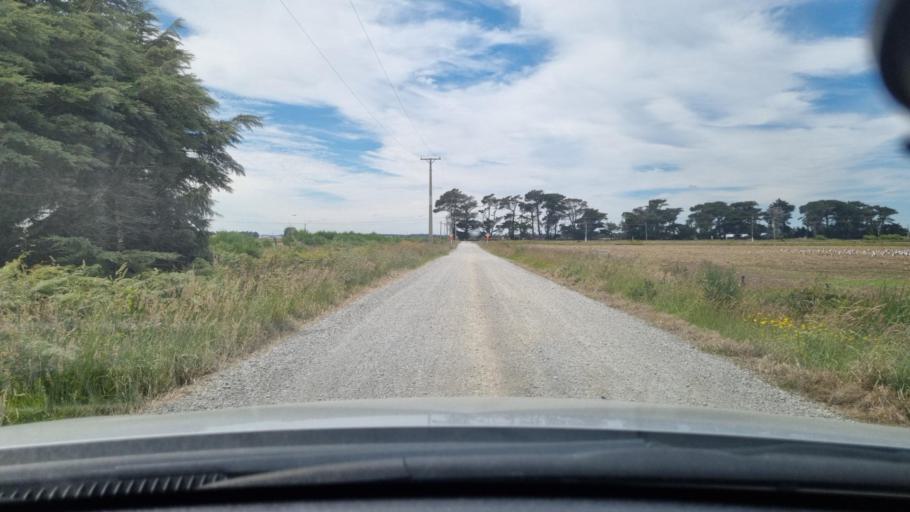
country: NZ
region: Southland
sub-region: Invercargill City
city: Invercargill
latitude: -46.4054
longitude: 168.2903
